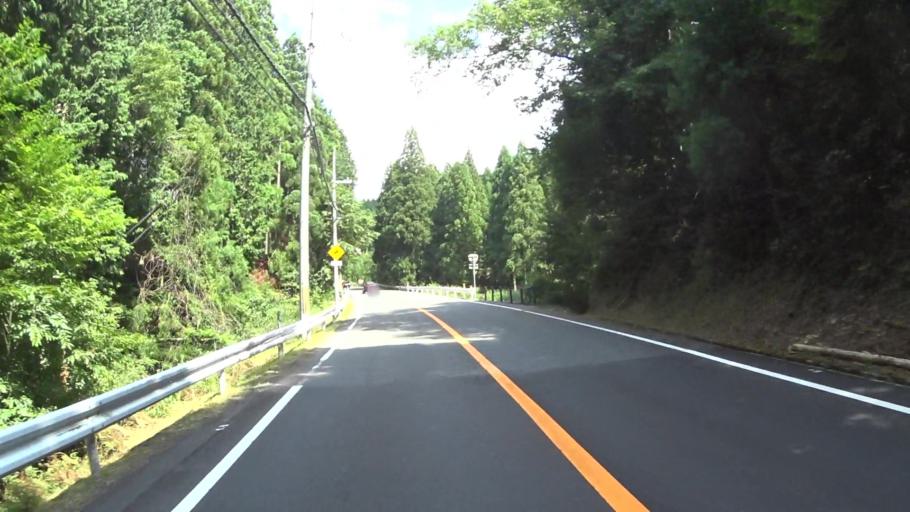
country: JP
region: Kyoto
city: Kameoka
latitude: 35.2764
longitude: 135.5638
